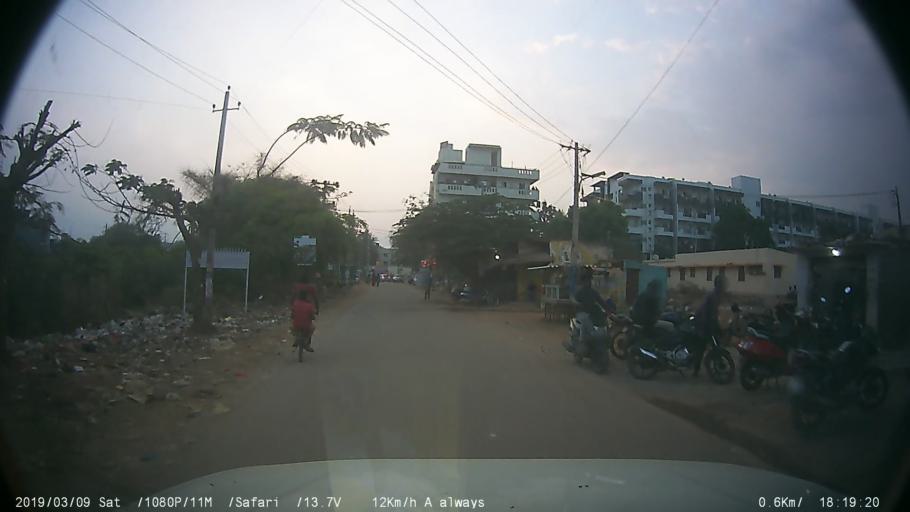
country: IN
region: Karnataka
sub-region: Bangalore Urban
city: Anekal
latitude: 12.8281
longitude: 77.6902
